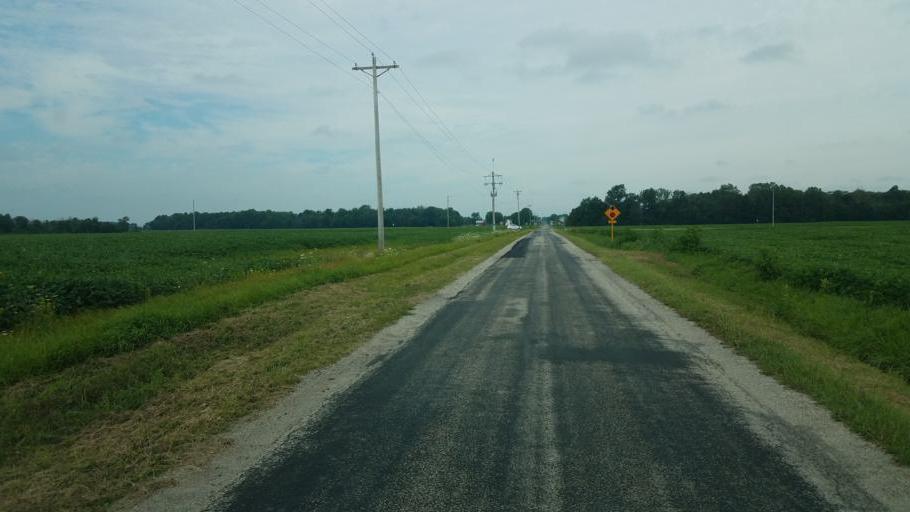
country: US
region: Ohio
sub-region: Morrow County
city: Cardington
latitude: 40.4998
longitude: -82.9605
